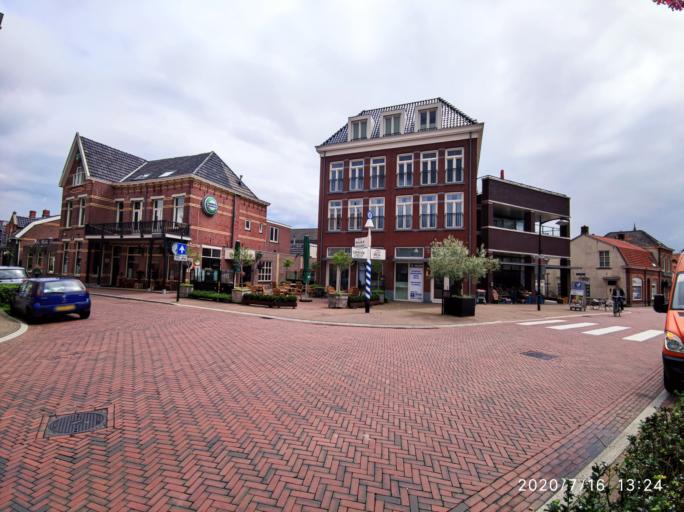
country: NL
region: North Brabant
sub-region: Gemeente Geertruidenberg
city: Geertruidenberg
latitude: 51.6962
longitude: 4.8744
